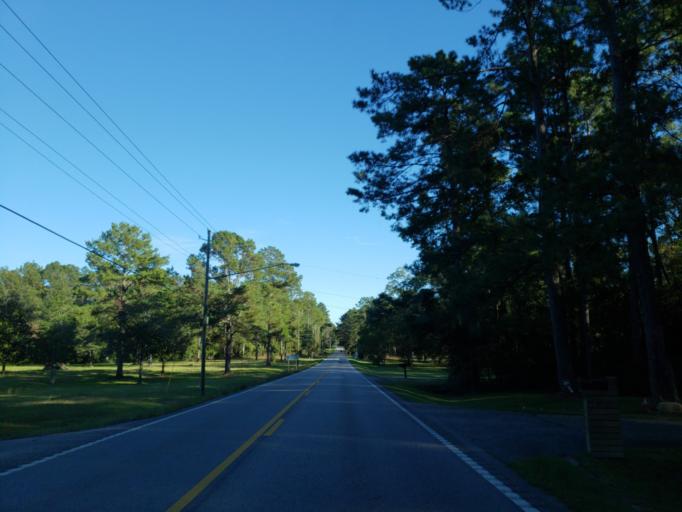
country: US
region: Mississippi
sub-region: Perry County
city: Richton
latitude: 31.3533
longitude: -88.9531
